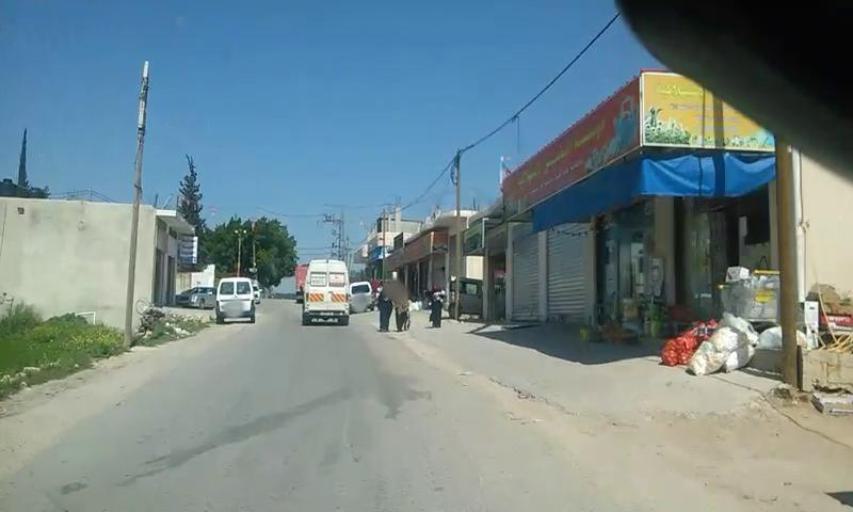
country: PS
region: West Bank
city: Al Majd
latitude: 31.4781
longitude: 34.9523
